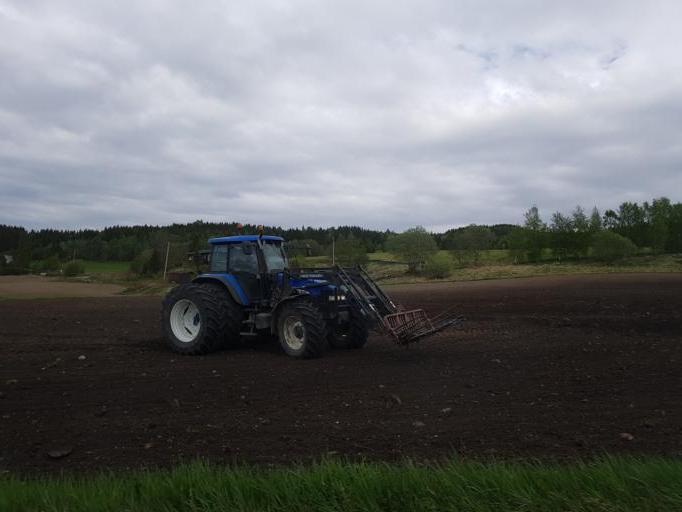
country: NO
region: Nord-Trondelag
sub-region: Levanger
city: Skogn
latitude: 63.7112
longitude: 11.2497
